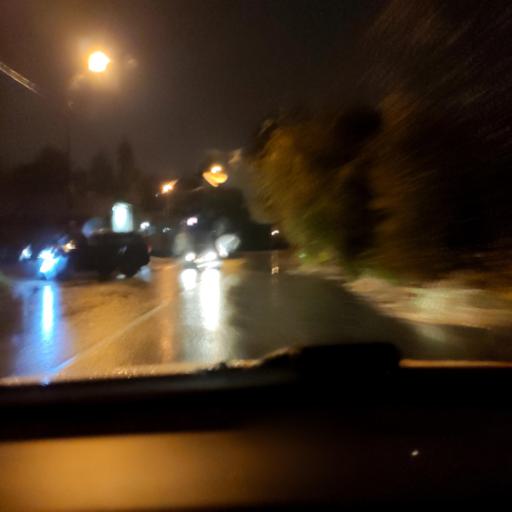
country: RU
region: Voronezj
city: Voronezh
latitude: 51.6450
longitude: 39.1734
